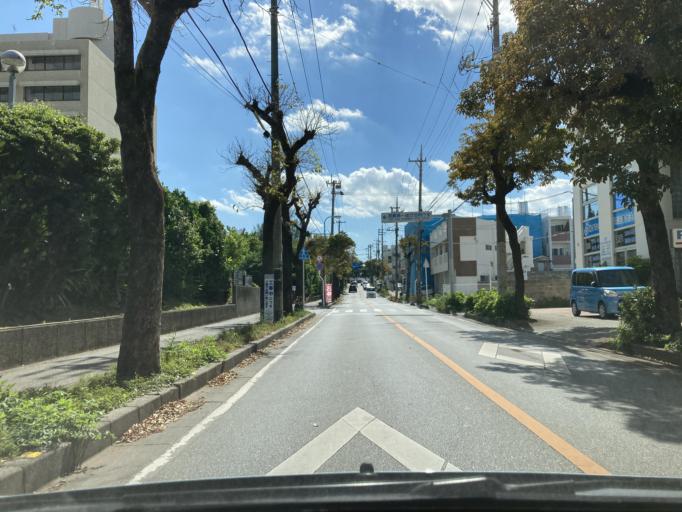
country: JP
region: Okinawa
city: Naha-shi
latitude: 26.2083
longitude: 127.6860
